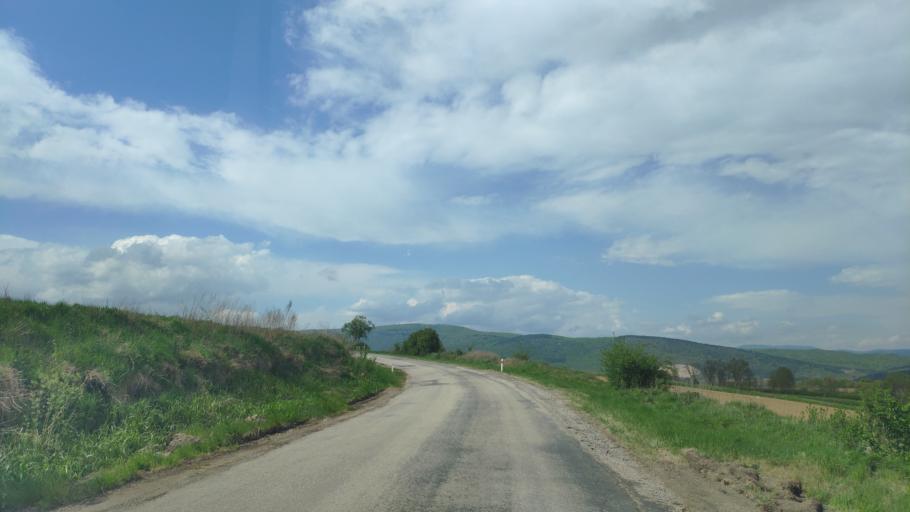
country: SK
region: Kosicky
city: Moldava nad Bodvou
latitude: 48.5788
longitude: 20.9292
